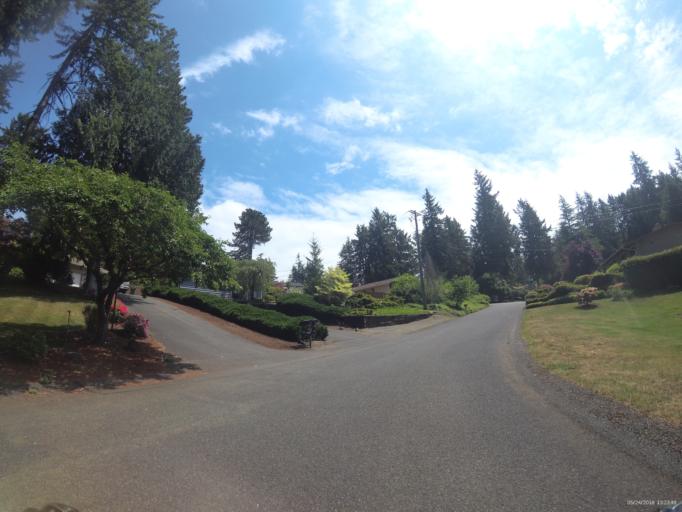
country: US
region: Washington
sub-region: Pierce County
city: Lakewood
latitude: 47.1847
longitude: -122.5295
